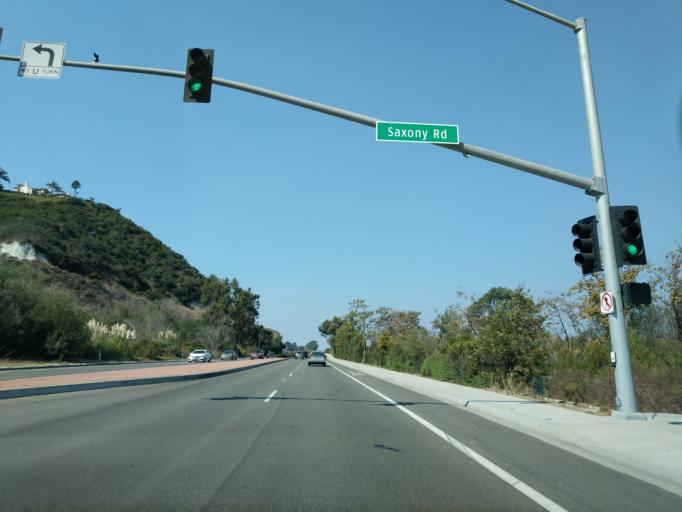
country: US
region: California
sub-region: San Diego County
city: Encinitas
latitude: 33.0873
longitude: -117.2873
